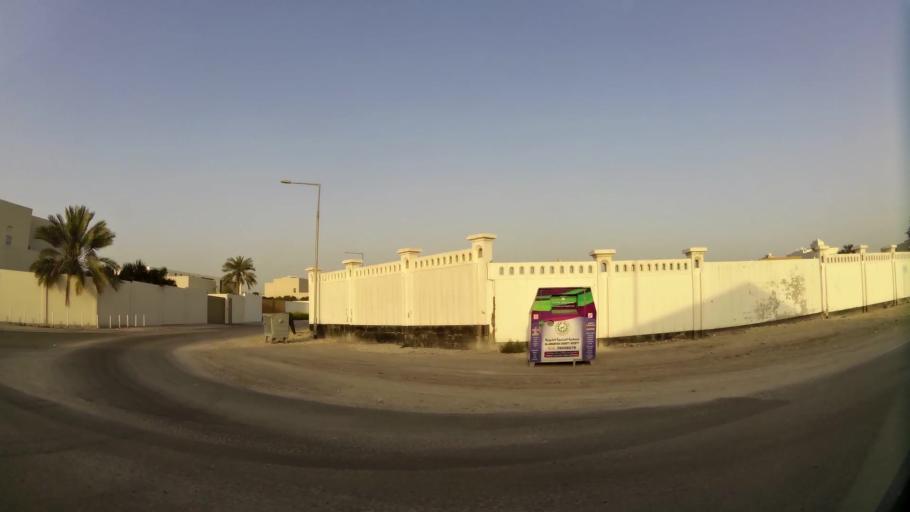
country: BH
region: Northern
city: Madinat `Isa
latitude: 26.1922
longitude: 50.4768
